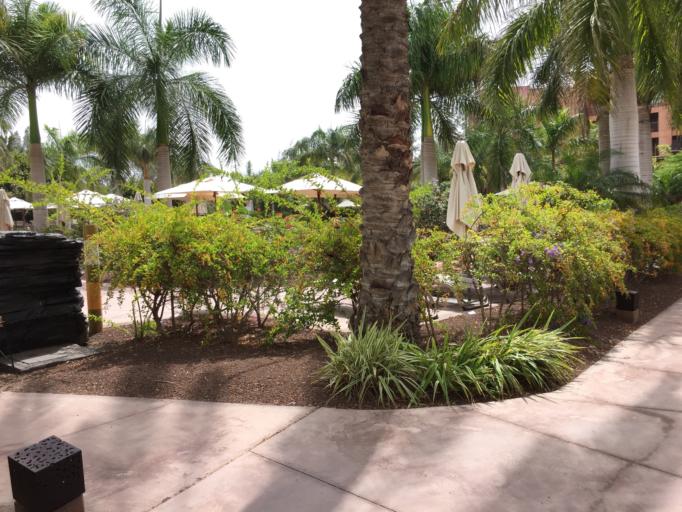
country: ES
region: Canary Islands
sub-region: Provincia de Las Palmas
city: Maspalomas
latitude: 27.7404
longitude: -15.5991
